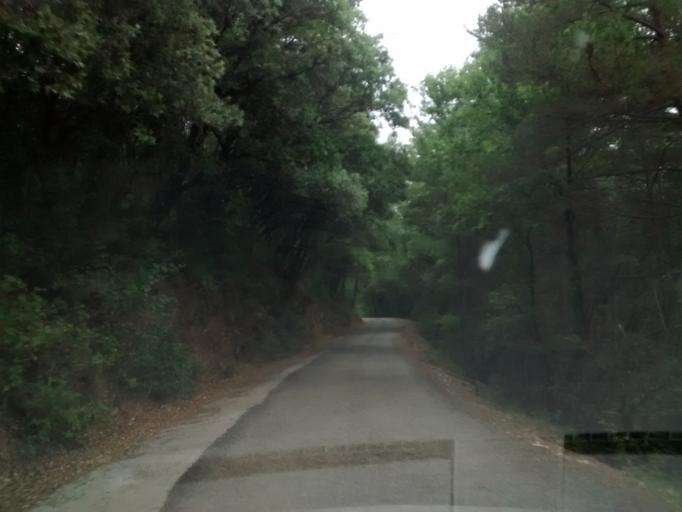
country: ES
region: Aragon
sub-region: Provincia de Huesca
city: Puertolas
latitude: 42.5306
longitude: 0.1309
